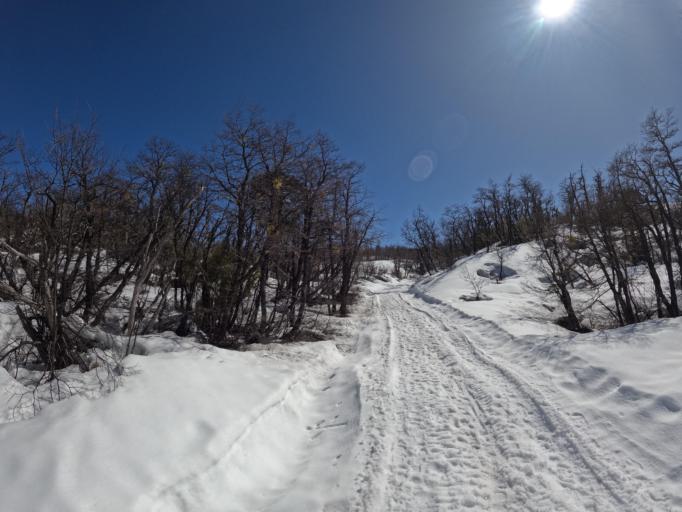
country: CL
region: Araucania
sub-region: Provincia de Cautin
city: Vilcun
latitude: -38.6610
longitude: -71.6185
